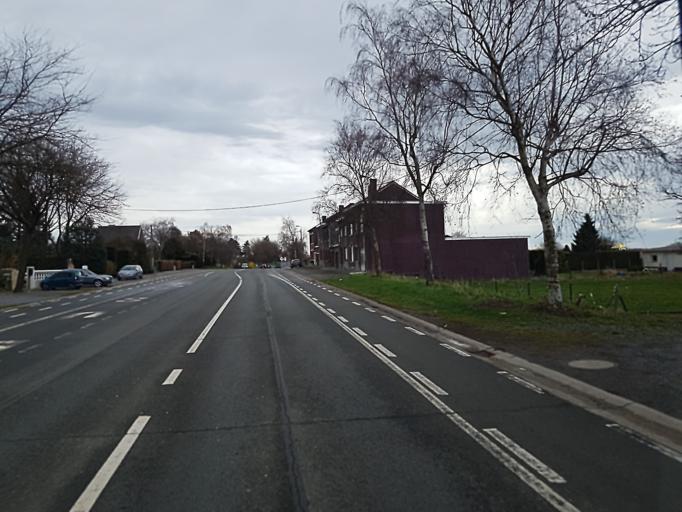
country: BE
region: Wallonia
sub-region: Province de Liege
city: Oreye
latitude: 50.7320
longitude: 5.3468
